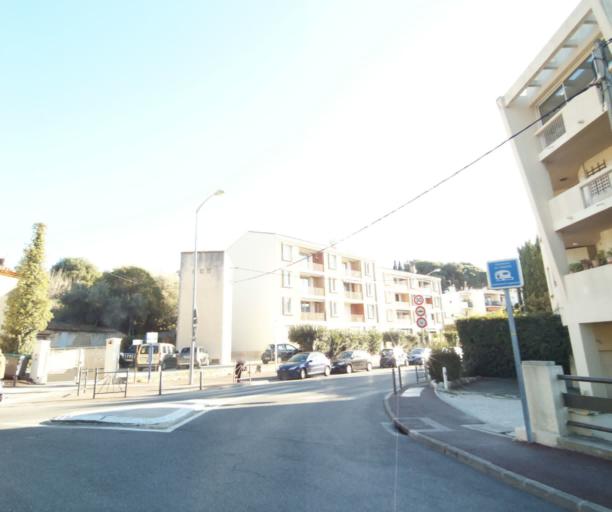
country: FR
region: Provence-Alpes-Cote d'Azur
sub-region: Departement des Bouches-du-Rhone
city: Cassis
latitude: 43.2151
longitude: 5.5437
